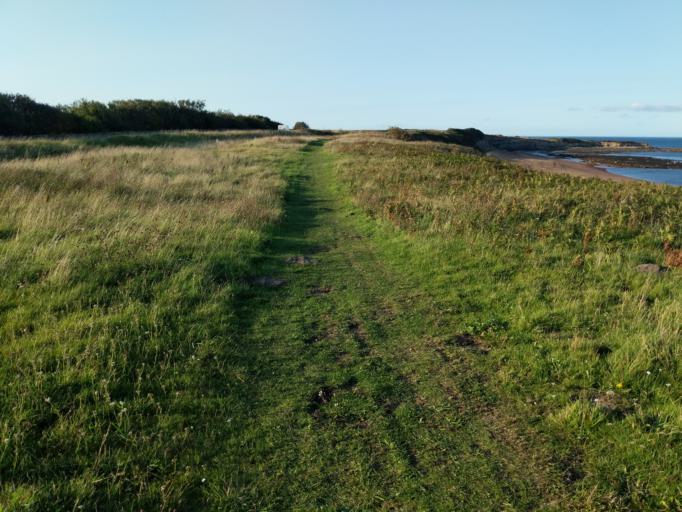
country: GB
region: England
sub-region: Northumberland
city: Lynemouth
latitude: 55.2212
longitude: -1.5298
